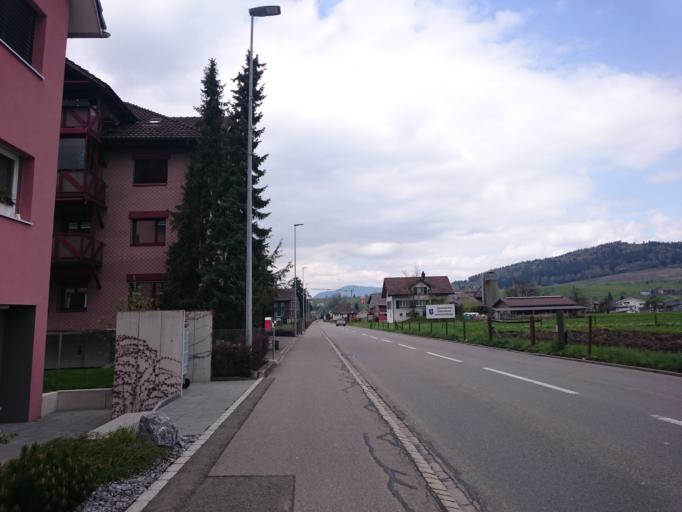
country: CH
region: Schwyz
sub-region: Bezirk March
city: Schubelbach
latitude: 47.1844
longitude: 8.8980
